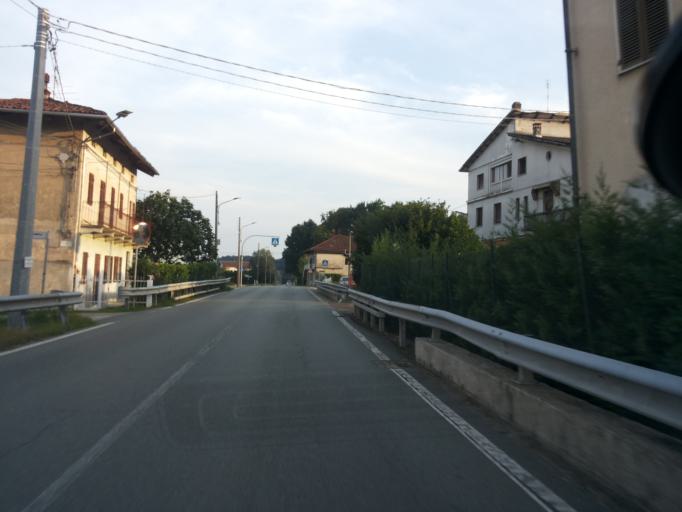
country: IT
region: Piedmont
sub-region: Provincia di Biella
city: Mottalciata
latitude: 45.5222
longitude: 8.1984
